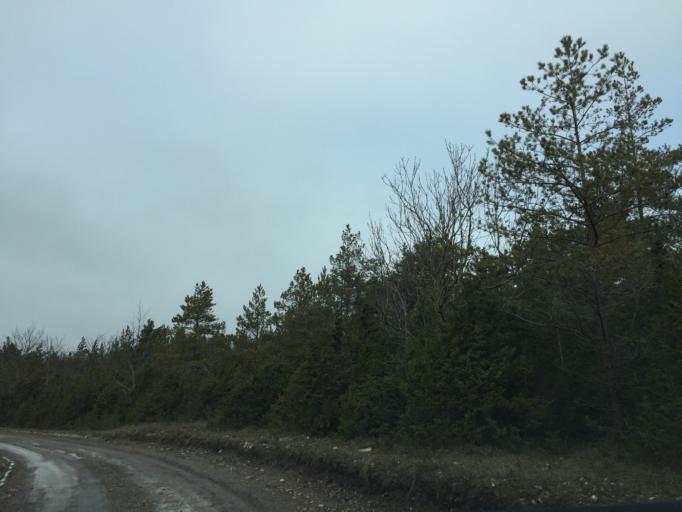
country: EE
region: Saare
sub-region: Kuressaare linn
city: Kuressaare
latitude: 58.4969
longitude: 21.9274
